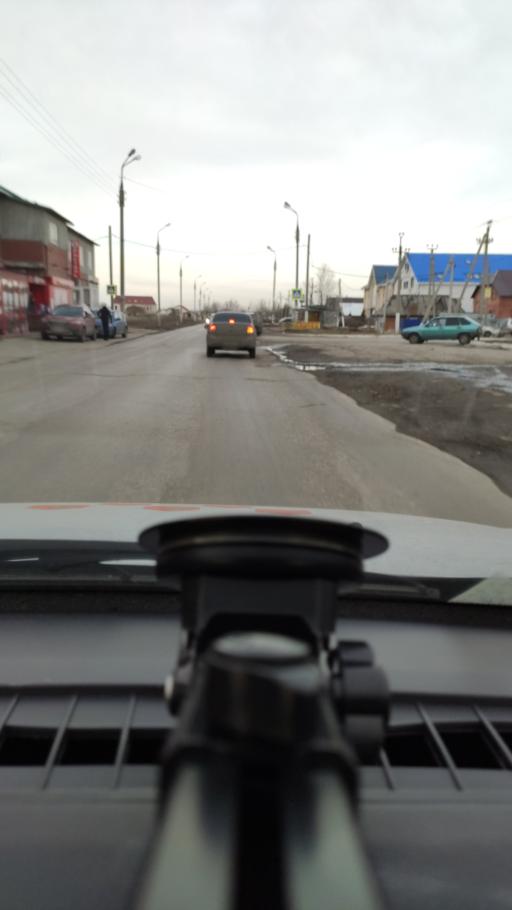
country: RU
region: Samara
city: Tol'yatti
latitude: 53.5662
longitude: 49.3968
